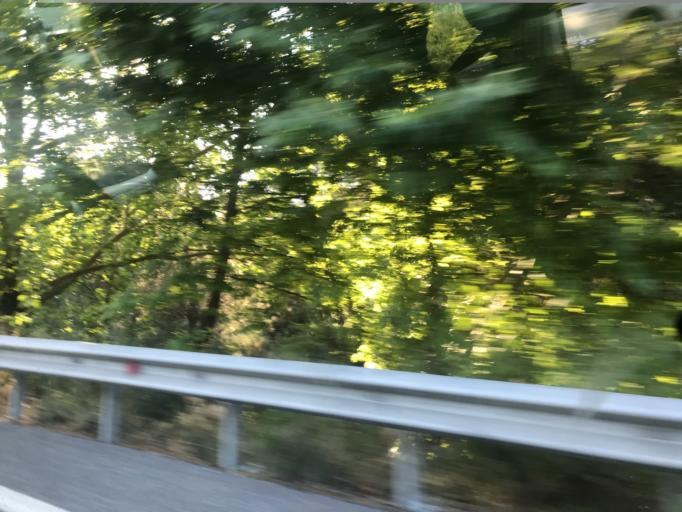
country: TR
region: Mugla
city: Ula
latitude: 37.0614
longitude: 28.3533
